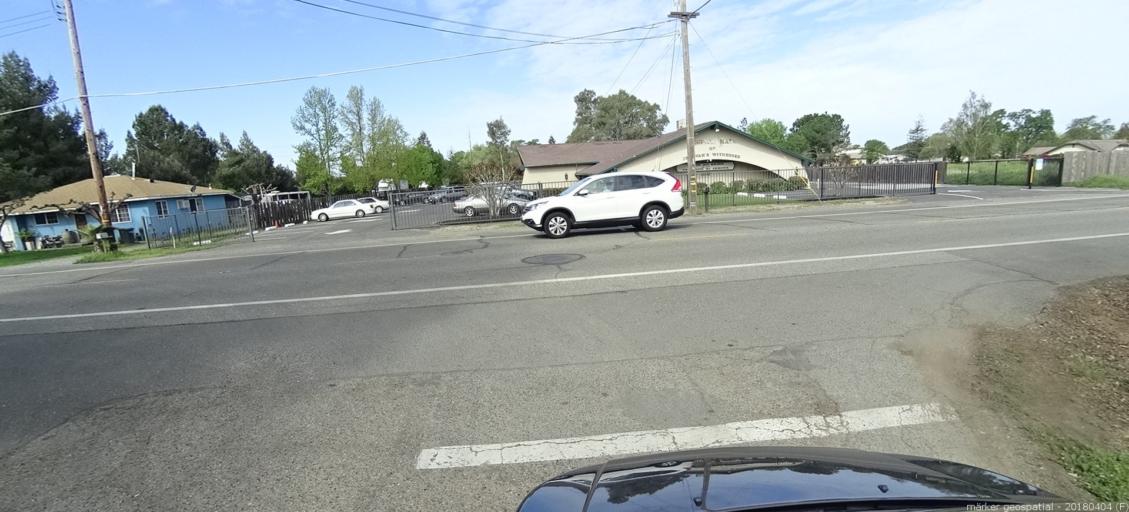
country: US
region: California
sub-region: Sacramento County
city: Galt
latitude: 38.2458
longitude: -121.2975
